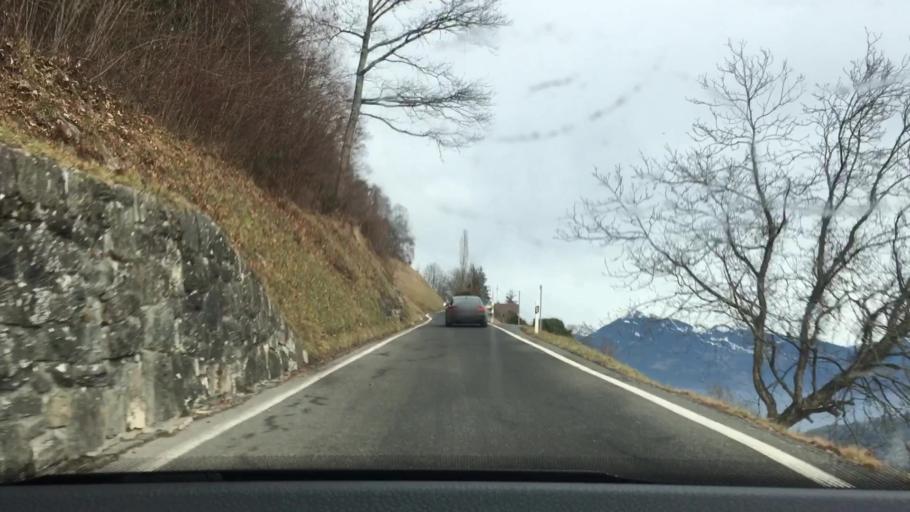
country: CH
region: Valais
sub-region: Monthey District
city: Troistorrents
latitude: 46.2244
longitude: 6.9076
